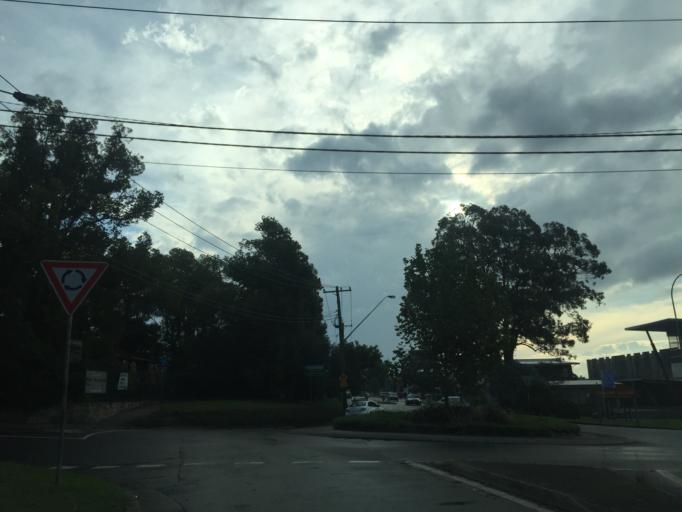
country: AU
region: New South Wales
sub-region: Hornsby Shire
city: Galston
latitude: -33.6533
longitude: 151.0474
